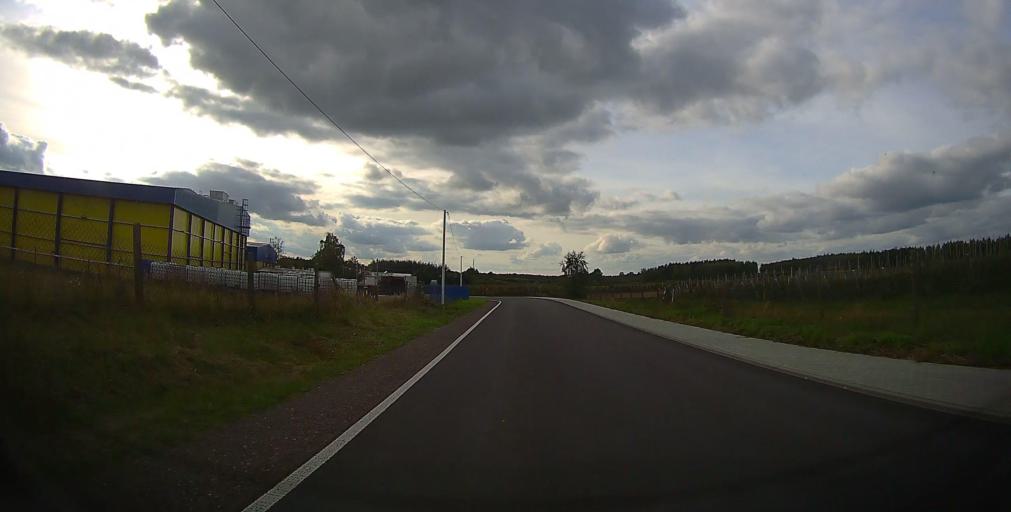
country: PL
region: Masovian Voivodeship
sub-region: Powiat bialobrzeski
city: Promna
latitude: 51.7119
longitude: 20.9548
